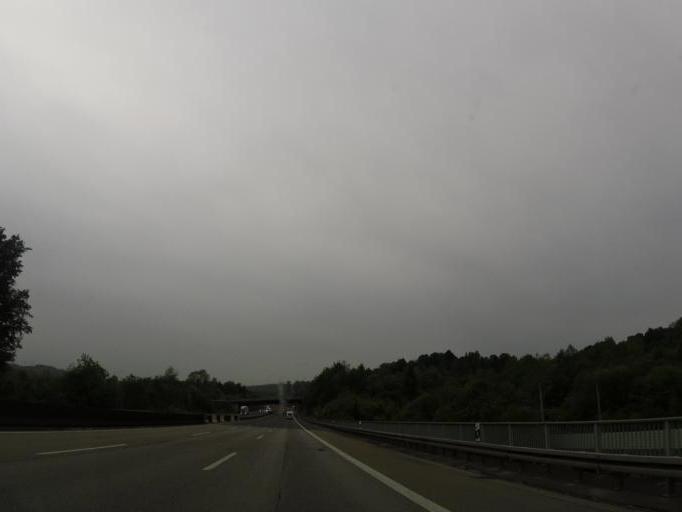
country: DE
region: Lower Saxony
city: Scheden
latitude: 51.4044
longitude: 9.7118
